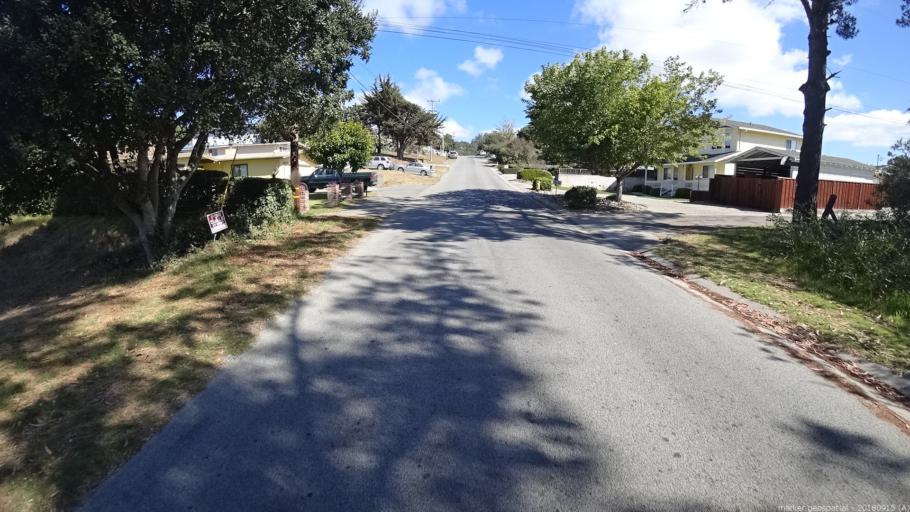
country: US
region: California
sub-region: Monterey County
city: Las Lomas
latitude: 36.8684
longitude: -121.7310
